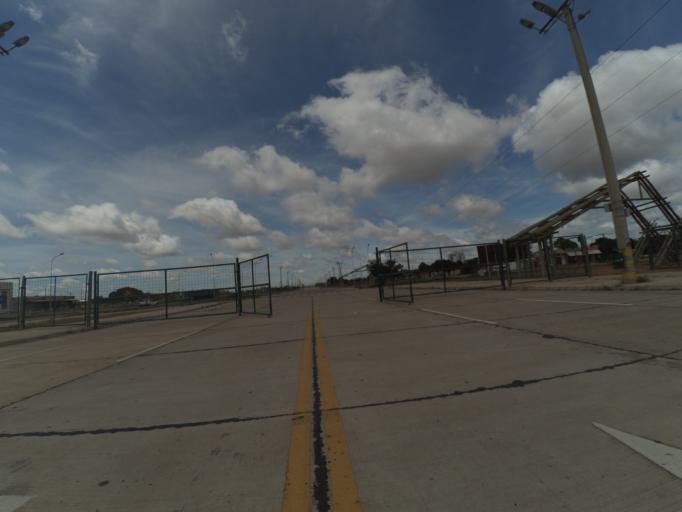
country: BO
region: Santa Cruz
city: Santa Cruz de la Sierra
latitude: -17.7354
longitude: -63.1412
